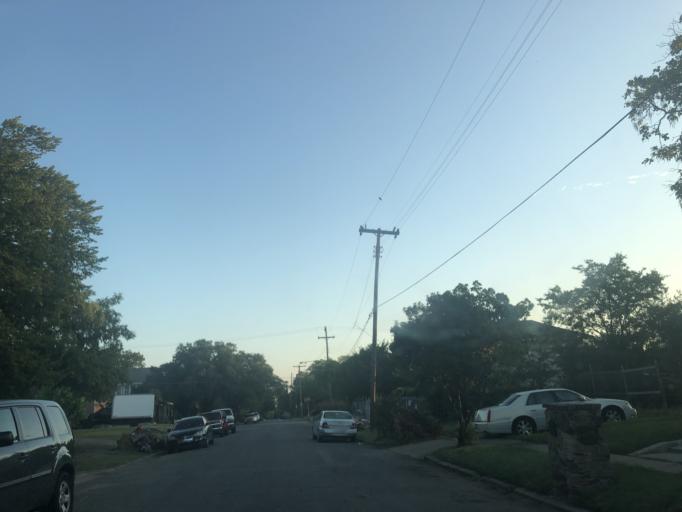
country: US
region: Texas
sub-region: Dallas County
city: Dallas
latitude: 32.7514
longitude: -96.8253
